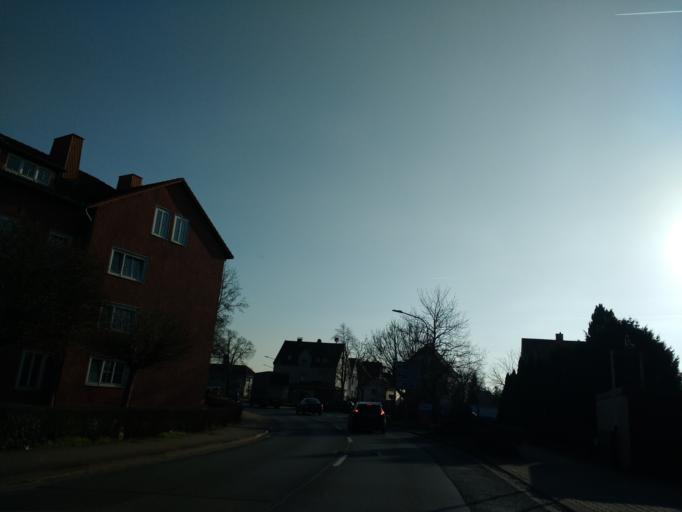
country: DE
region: Lower Saxony
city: Hessisch Oldendorf
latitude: 52.1712
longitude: 9.2527
